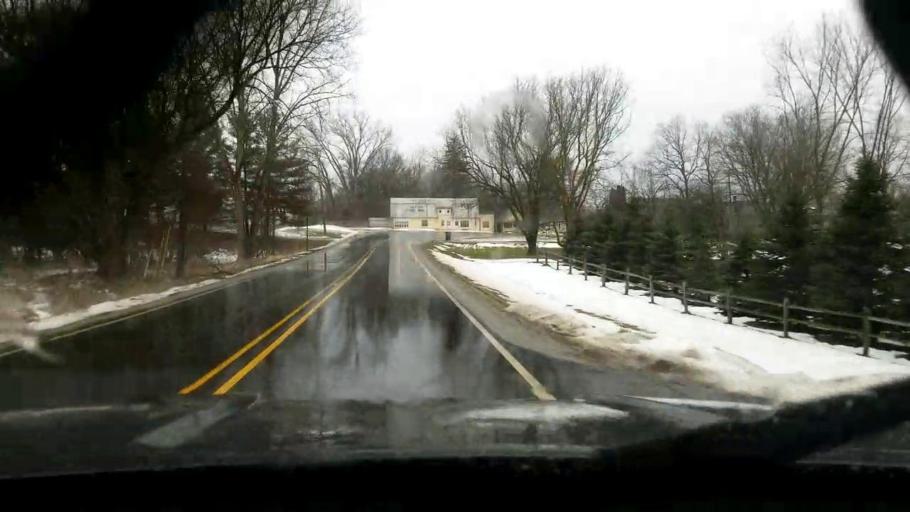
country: US
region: Michigan
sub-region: Jackson County
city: Michigan Center
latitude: 42.2929
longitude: -84.3190
